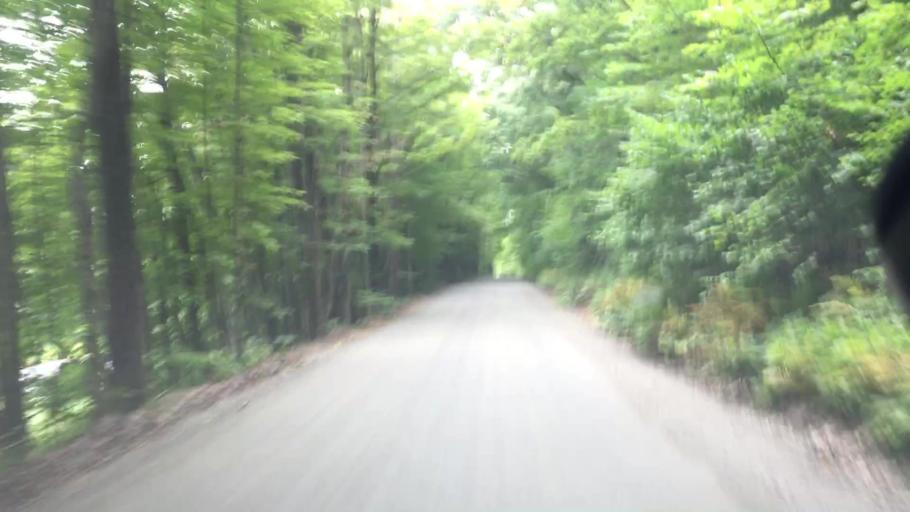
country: US
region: Vermont
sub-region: Windham County
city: Dover
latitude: 42.8544
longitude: -72.7783
